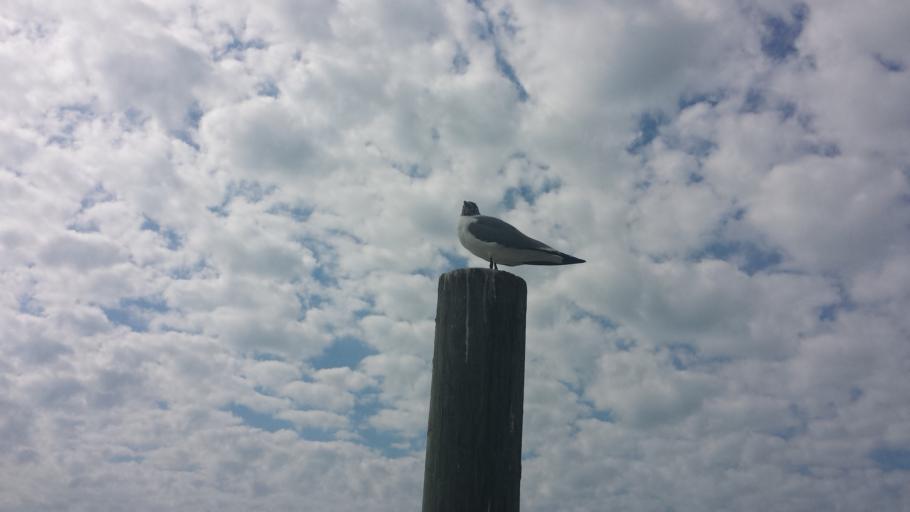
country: US
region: Florida
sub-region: Manatee County
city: Cortez
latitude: 27.4700
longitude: -82.6906
